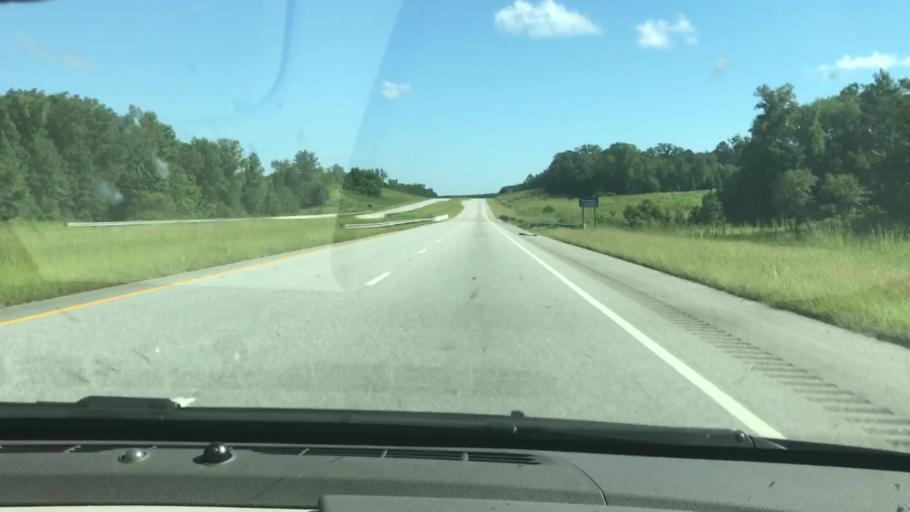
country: US
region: Alabama
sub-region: Russell County
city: Ladonia
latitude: 32.2000
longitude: -85.1765
